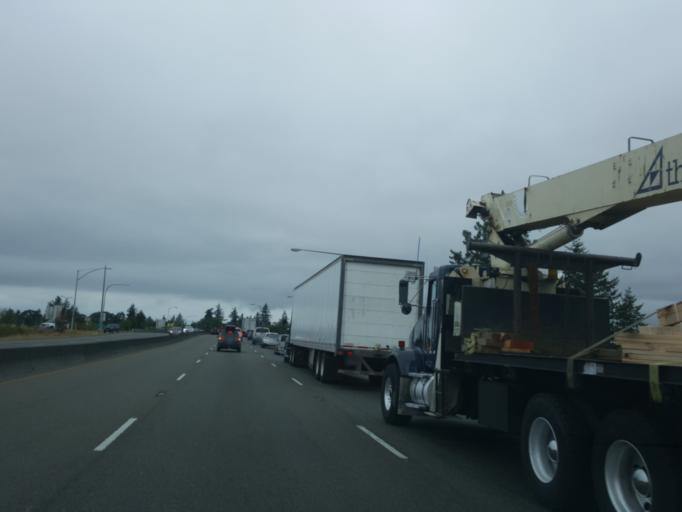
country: US
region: Washington
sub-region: Pierce County
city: McChord Air Force Base
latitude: 47.1625
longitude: -122.4771
